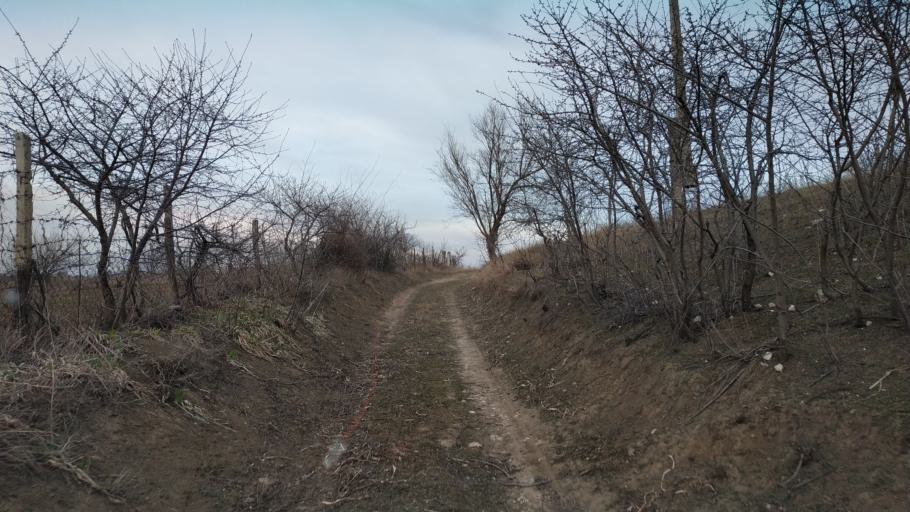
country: MD
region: Hincesti
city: Dancu
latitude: 46.7501
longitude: 28.2101
